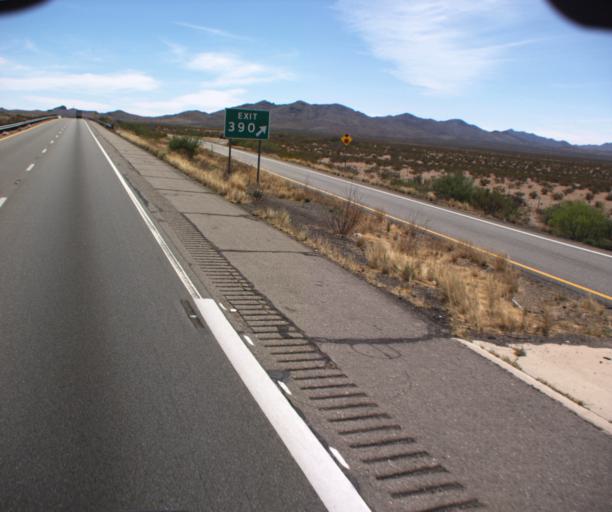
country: US
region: New Mexico
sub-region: Hidalgo County
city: Lordsburg
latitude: 32.2296
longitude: -109.0582
